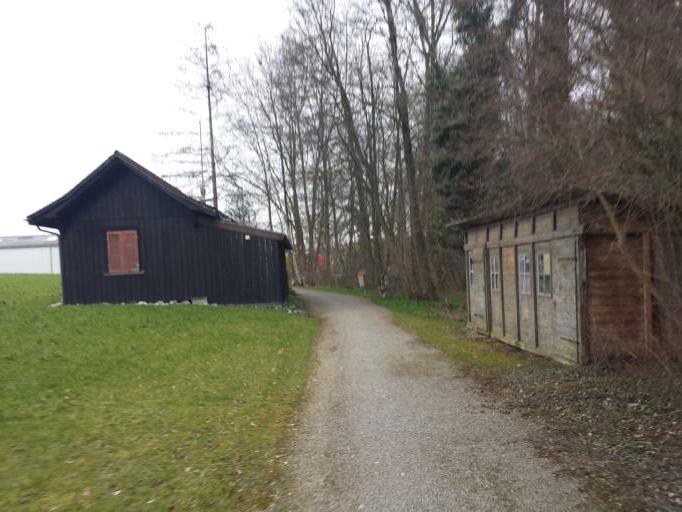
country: CH
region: Thurgau
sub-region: Arbon District
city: Salmsach
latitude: 47.5563
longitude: 9.3658
